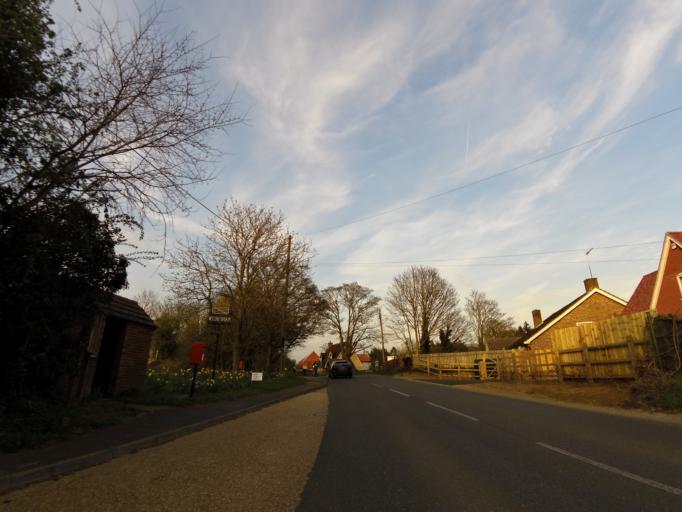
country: GB
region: England
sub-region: Suffolk
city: Ipswich
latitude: 52.1073
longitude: 1.1887
